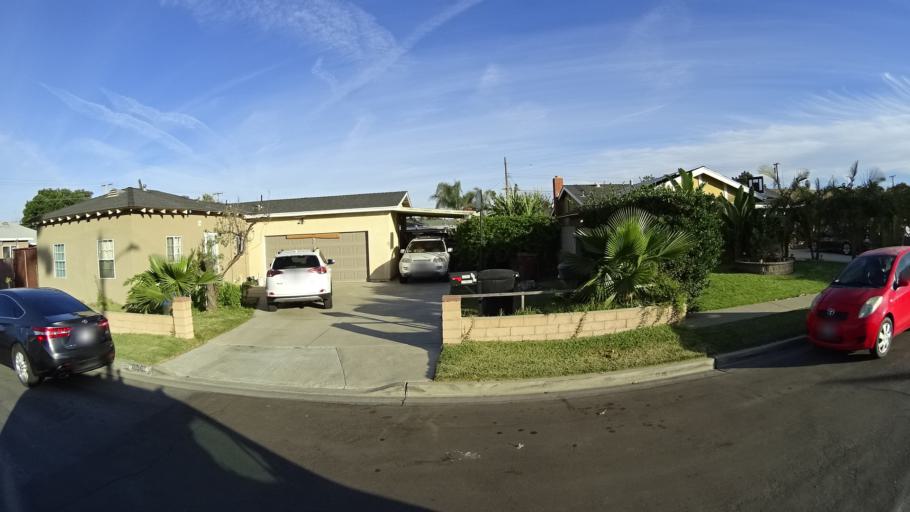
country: US
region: California
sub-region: Orange County
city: Garden Grove
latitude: 33.7689
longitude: -117.9478
